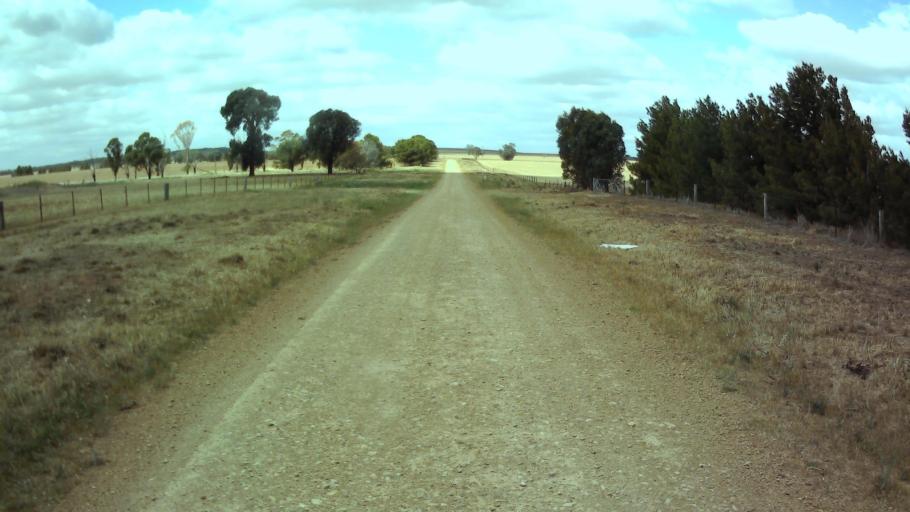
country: AU
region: New South Wales
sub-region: Weddin
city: Grenfell
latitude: -34.0616
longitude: 148.3300
